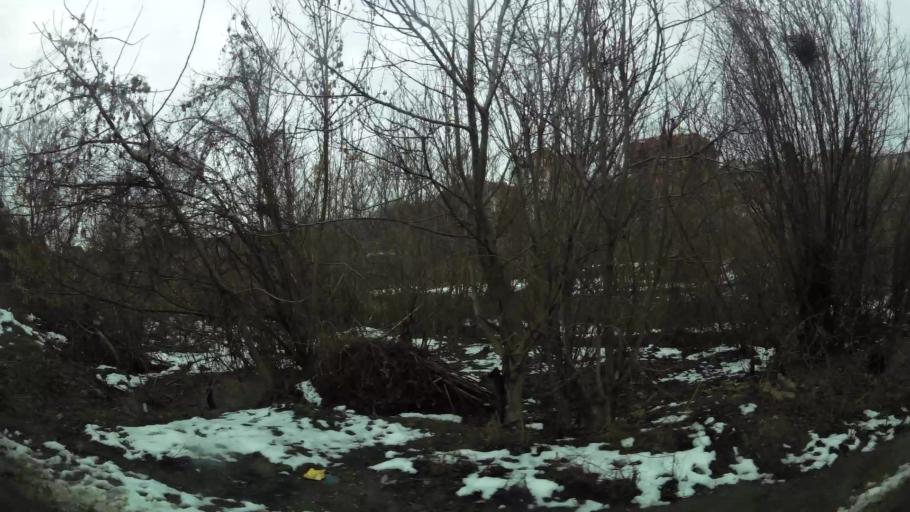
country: RS
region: Central Serbia
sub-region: Belgrade
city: Cukarica
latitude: 44.7565
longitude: 20.4076
